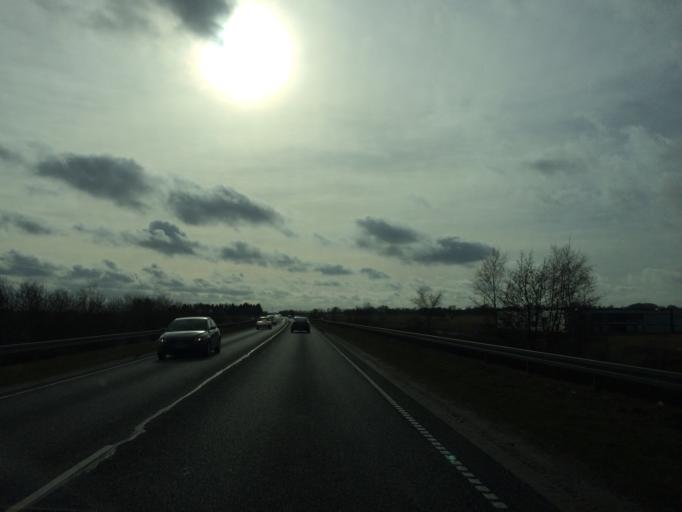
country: DK
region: Central Jutland
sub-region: Randers Kommune
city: Assentoft
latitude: 56.4368
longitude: 10.1617
